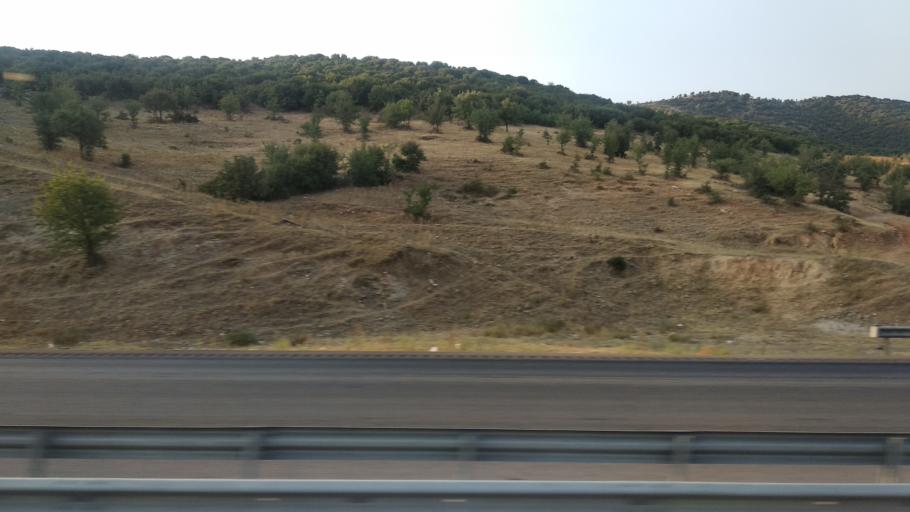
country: TR
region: Manisa
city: Menye
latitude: 38.5526
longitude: 28.4654
